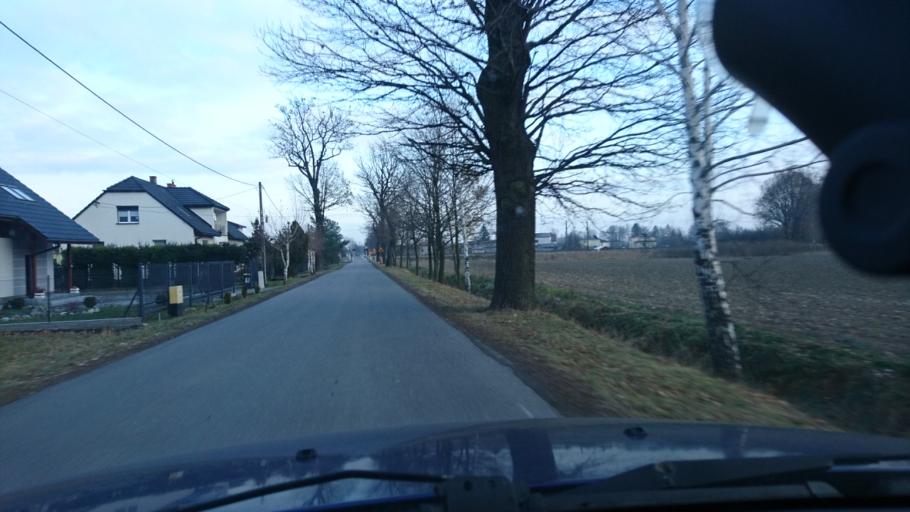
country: PL
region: Silesian Voivodeship
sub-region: Powiat bielski
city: Bestwinka
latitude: 49.9331
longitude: 19.0675
